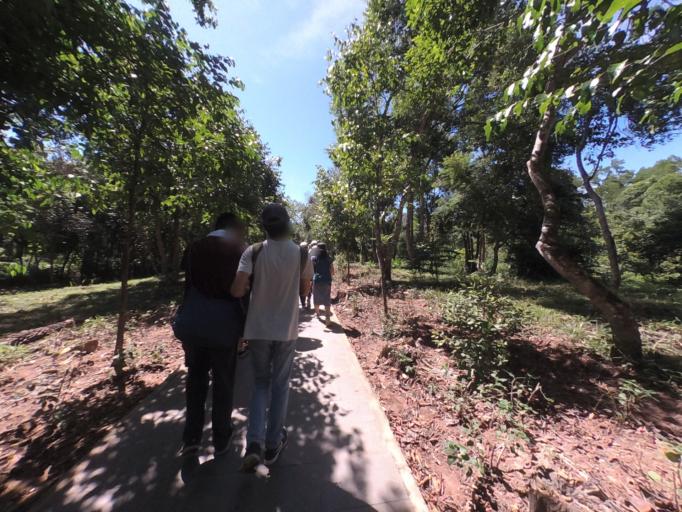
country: VN
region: Quang Nam
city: Dai Loc
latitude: 15.7662
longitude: 108.1226
